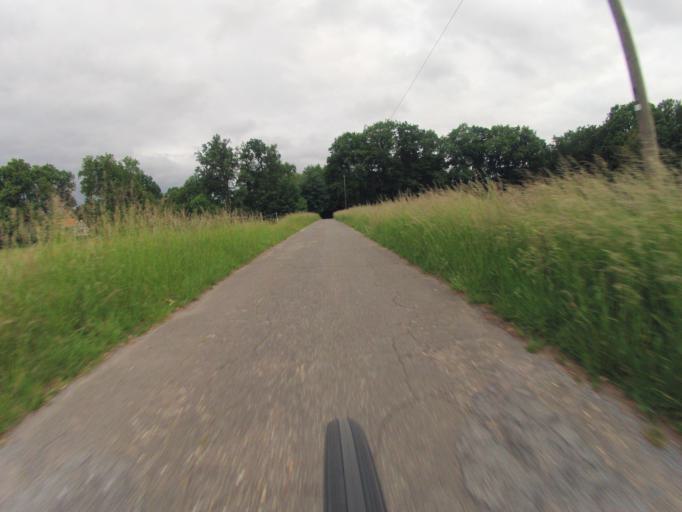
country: DE
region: North Rhine-Westphalia
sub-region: Regierungsbezirk Munster
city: Horstel
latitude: 52.2453
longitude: 7.5419
